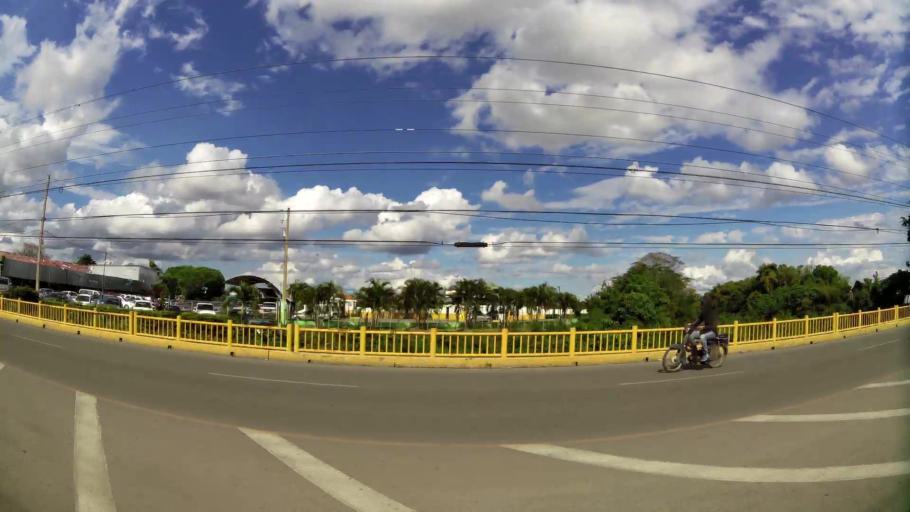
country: DO
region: La Vega
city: Concepcion de La Vega
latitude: 19.2312
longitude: -70.5287
